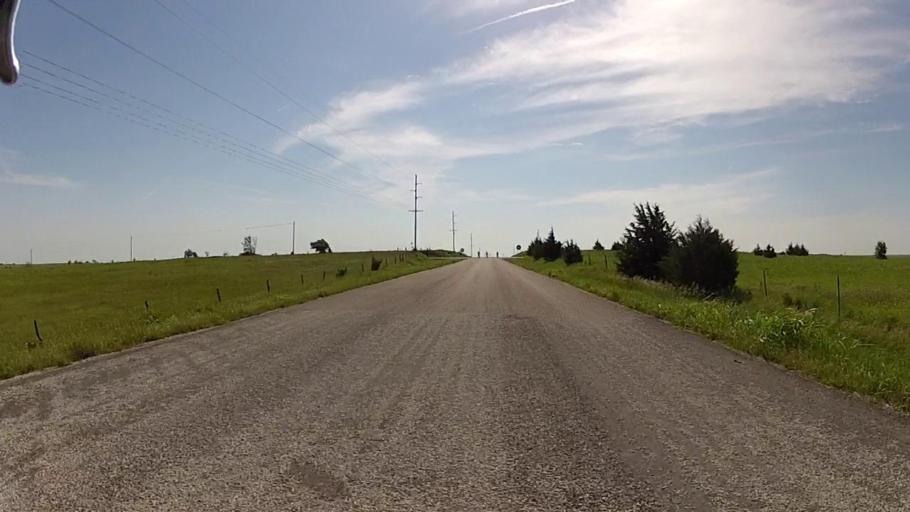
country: US
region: Kansas
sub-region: Cowley County
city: Winfield
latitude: 37.0712
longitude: -96.6450
